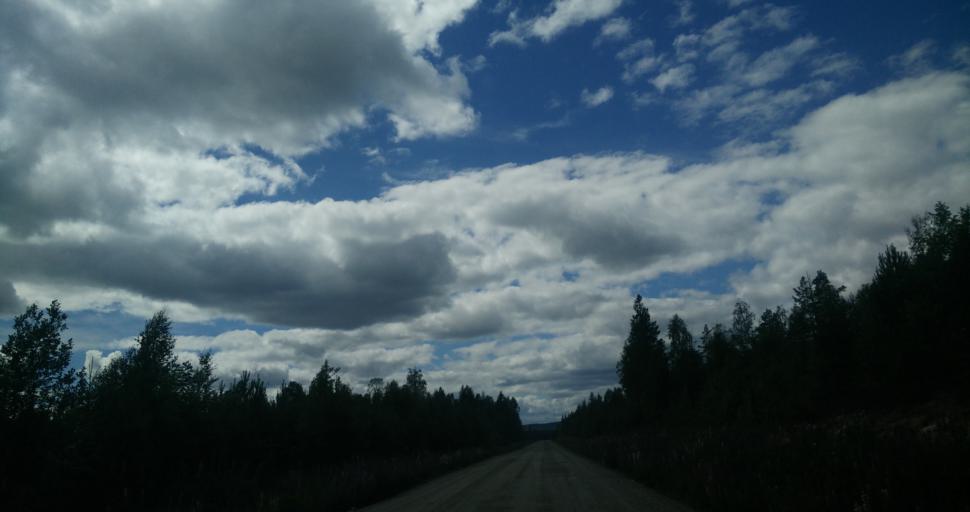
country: SE
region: Gaevleborg
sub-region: Nordanstigs Kommun
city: Bergsjoe
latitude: 62.1275
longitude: 17.1201
